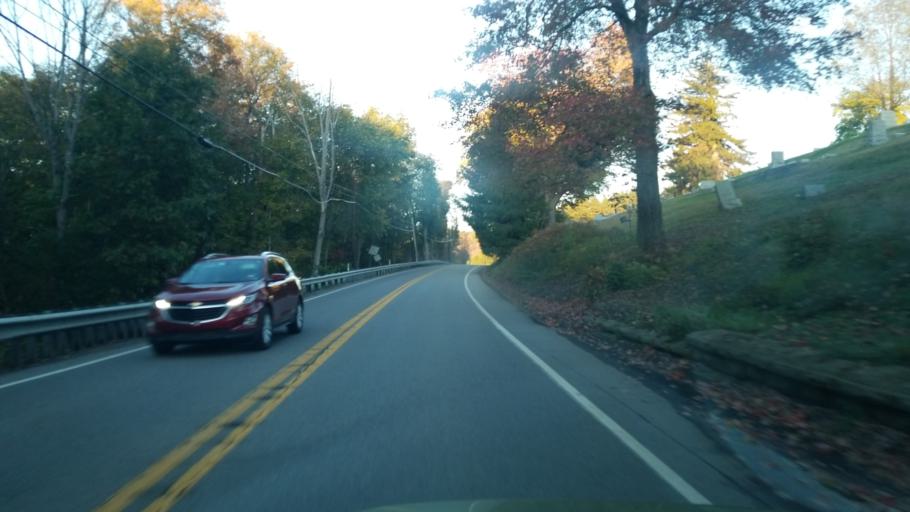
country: US
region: Pennsylvania
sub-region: Jefferson County
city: Reynoldsville
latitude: 41.0842
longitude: -78.8937
